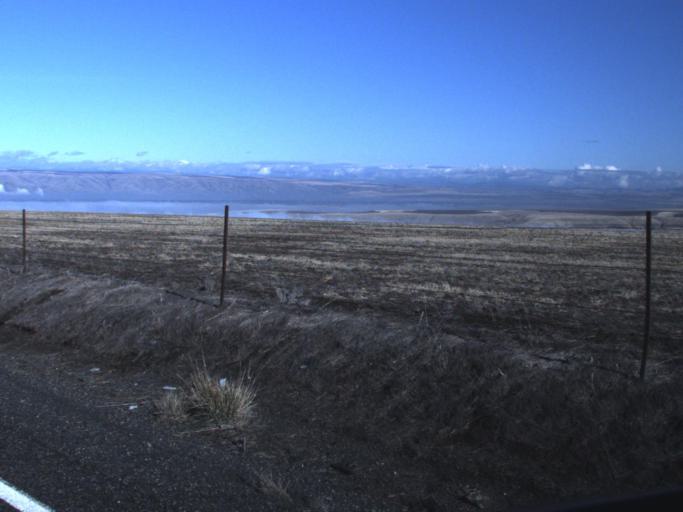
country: US
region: Washington
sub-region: Asotin County
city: Asotin
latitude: 46.3002
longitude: -117.0435
